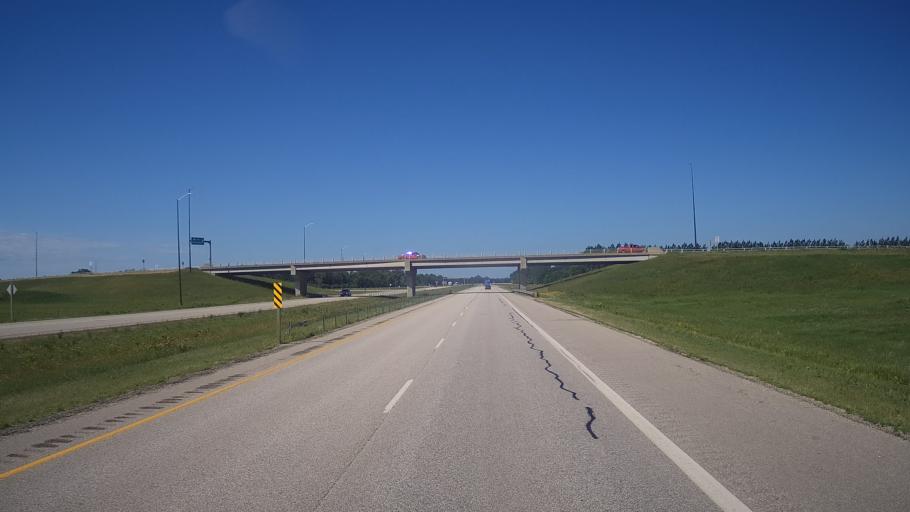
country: CA
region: Manitoba
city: Portage la Prairie
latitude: 49.9551
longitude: -98.2722
